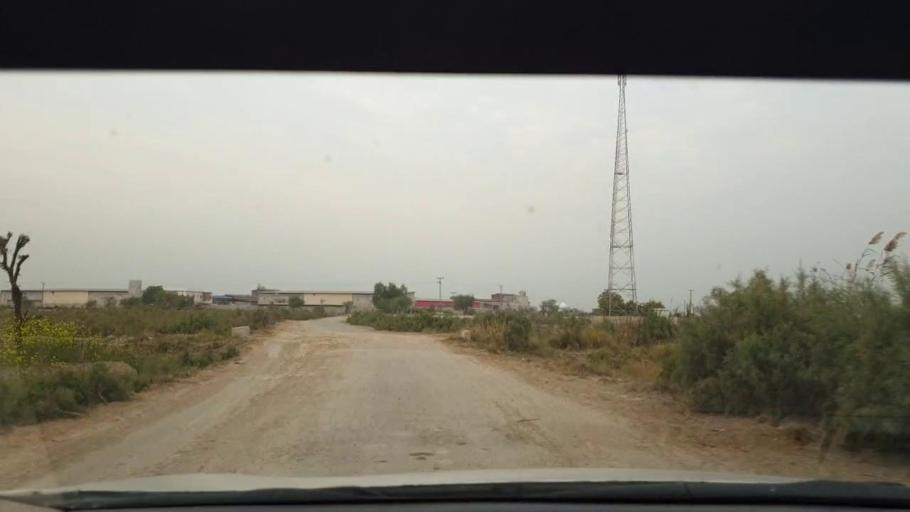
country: PK
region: Sindh
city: Sinjhoro
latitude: 25.9361
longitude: 68.7518
